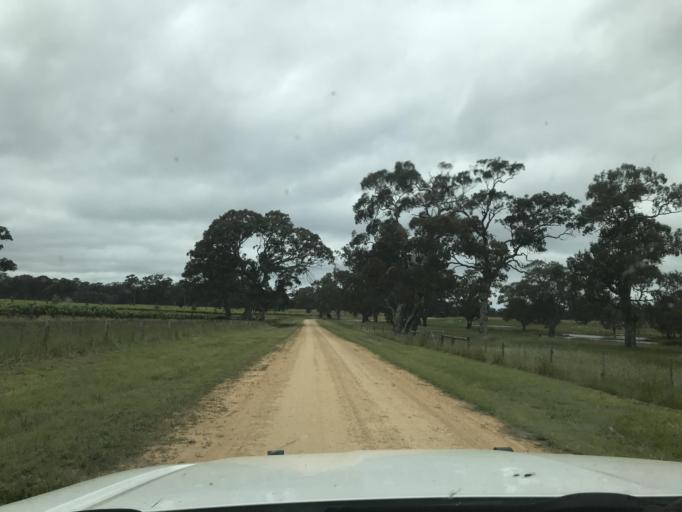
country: AU
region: South Australia
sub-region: Wattle Range
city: Penola
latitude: -37.2758
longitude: 140.9874
